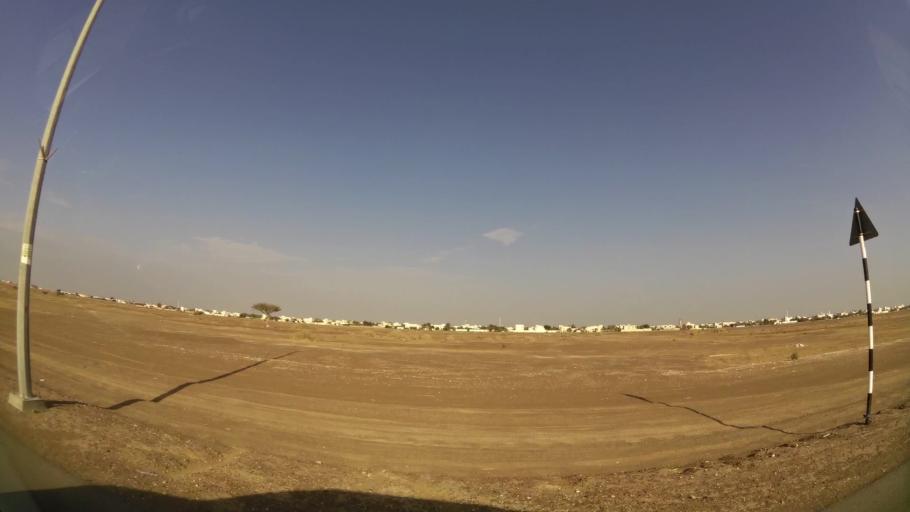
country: AE
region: Abu Dhabi
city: Al Ain
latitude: 24.0771
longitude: 55.8548
